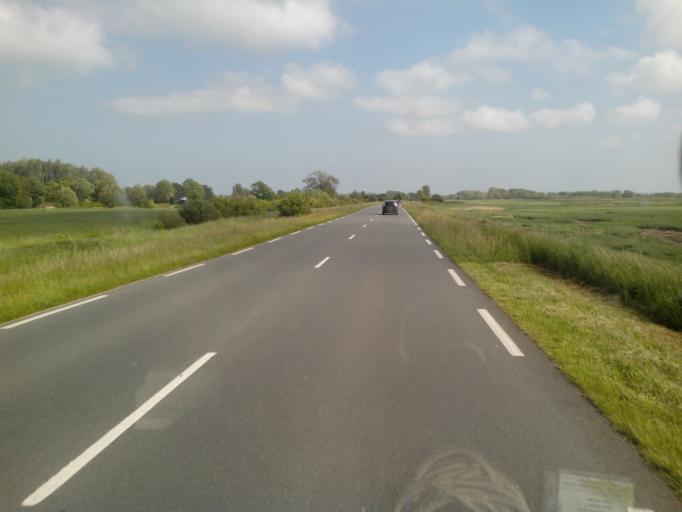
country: FR
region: Picardie
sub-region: Departement de la Somme
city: Saint-Valery-sur-Somme
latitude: 50.2071
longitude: 1.6808
